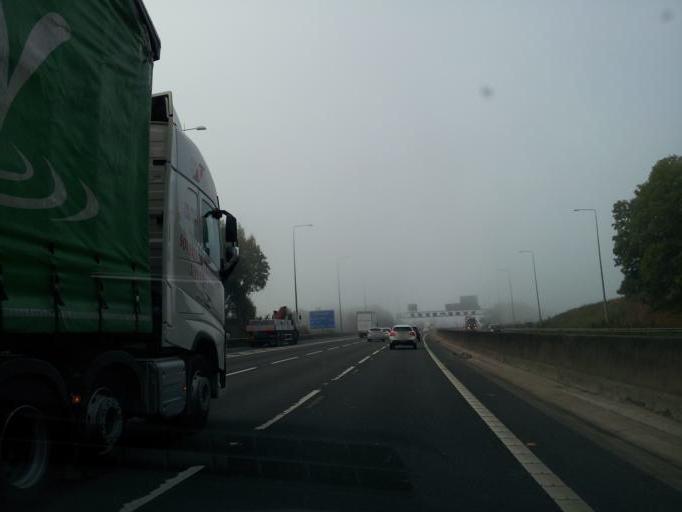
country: GB
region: England
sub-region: Kirklees
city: Cleckheaton
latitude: 53.7277
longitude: -1.7338
